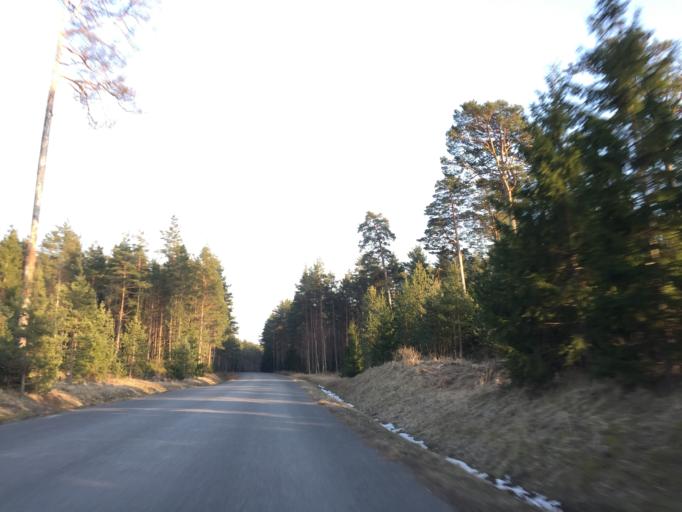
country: EE
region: Laeaene
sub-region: Lihula vald
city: Lihula
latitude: 58.4704
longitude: 23.7138
